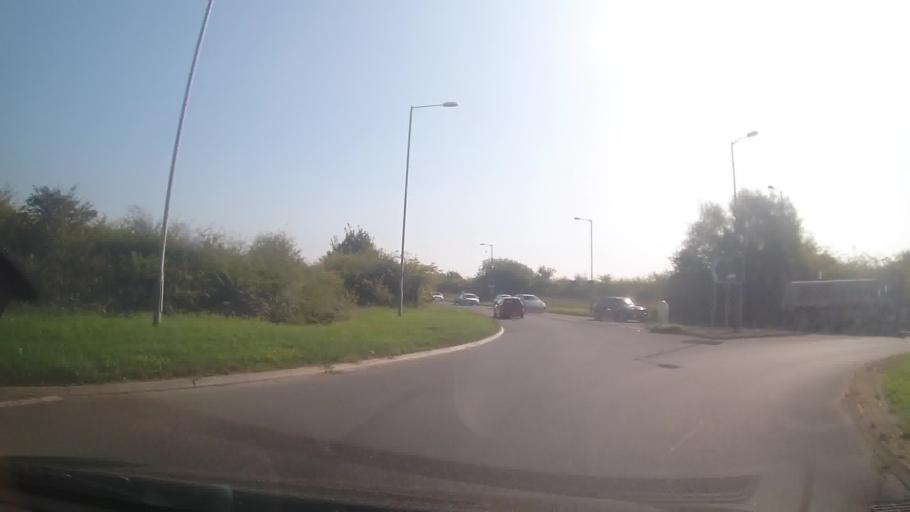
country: GB
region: England
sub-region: Worcestershire
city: Pershore
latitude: 52.1289
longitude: -2.0466
